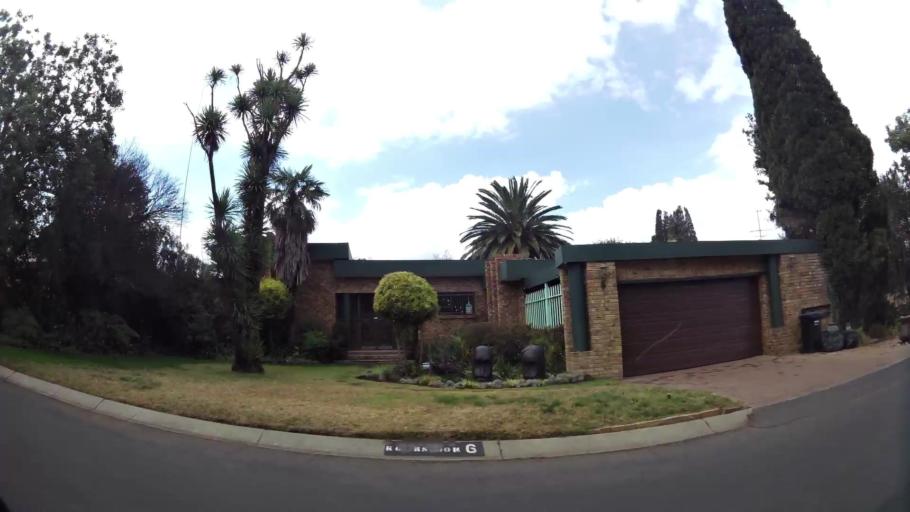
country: ZA
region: Gauteng
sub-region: Sedibeng District Municipality
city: Vanderbijlpark
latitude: -26.7389
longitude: 27.8529
